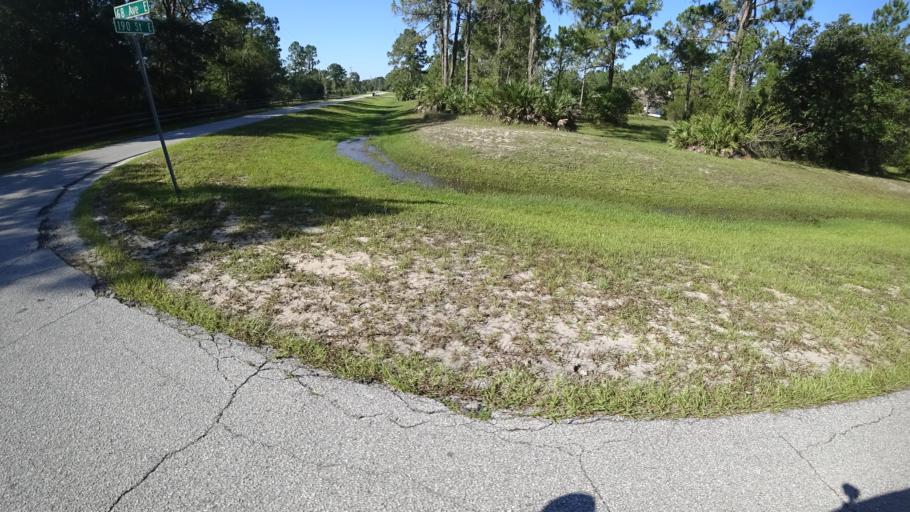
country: US
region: Florida
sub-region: Sarasota County
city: The Meadows
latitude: 27.4189
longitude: -82.3473
